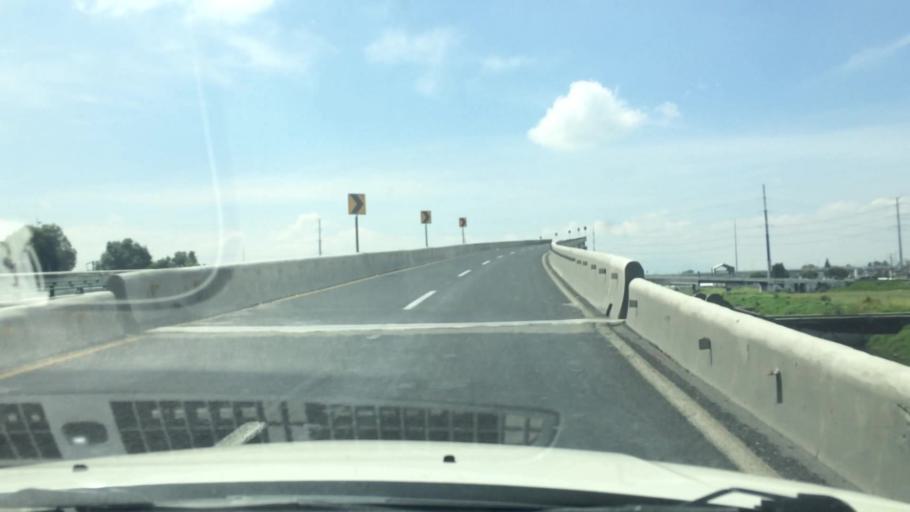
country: MX
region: Morelos
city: Lerma de Villada
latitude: 19.2869
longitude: -99.5216
